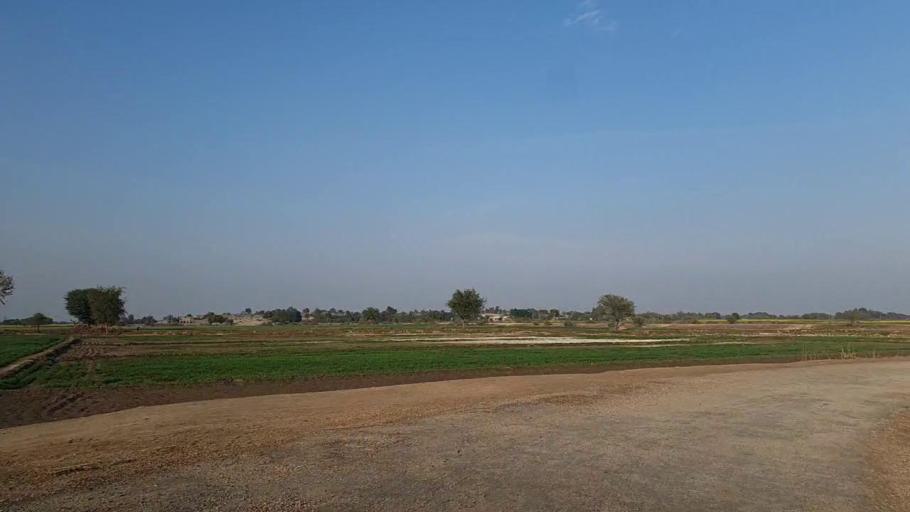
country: PK
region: Sindh
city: Jam Sahib
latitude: 26.3768
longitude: 68.5274
